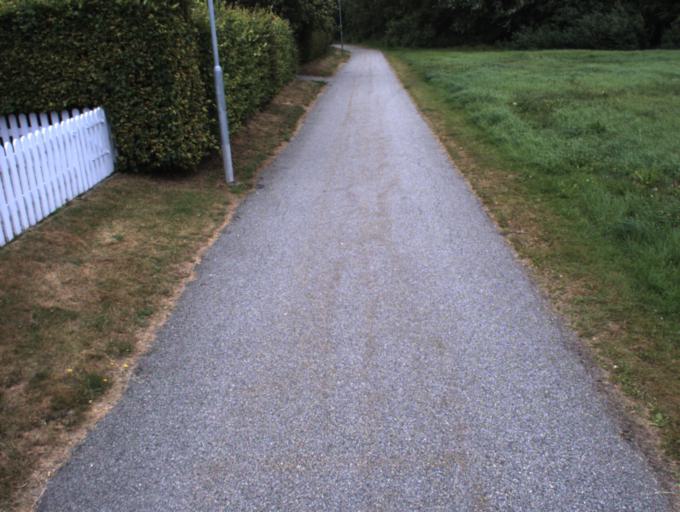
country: SE
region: Skane
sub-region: Helsingborg
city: Rydeback
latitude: 56.0030
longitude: 12.7590
